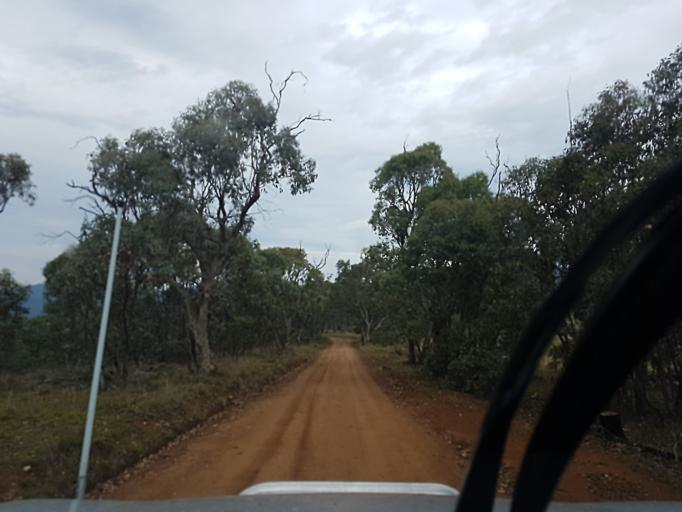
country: AU
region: New South Wales
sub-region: Snowy River
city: Jindabyne
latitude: -36.9585
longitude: 148.3742
